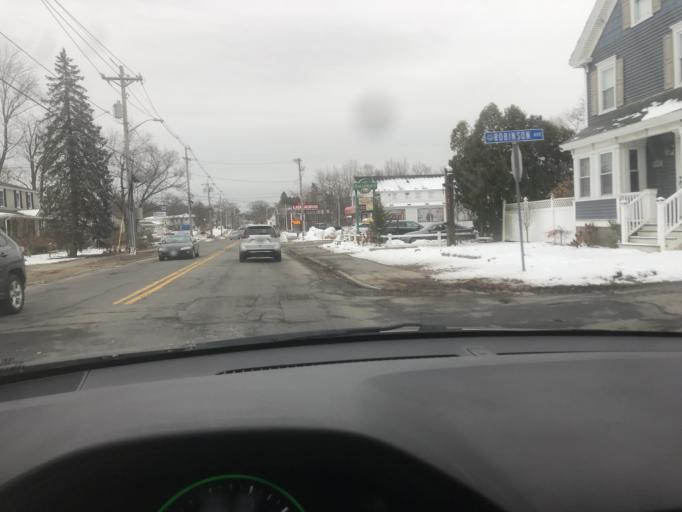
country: US
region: Massachusetts
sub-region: Middlesex County
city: Tewksbury
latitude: 42.6109
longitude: -71.2318
